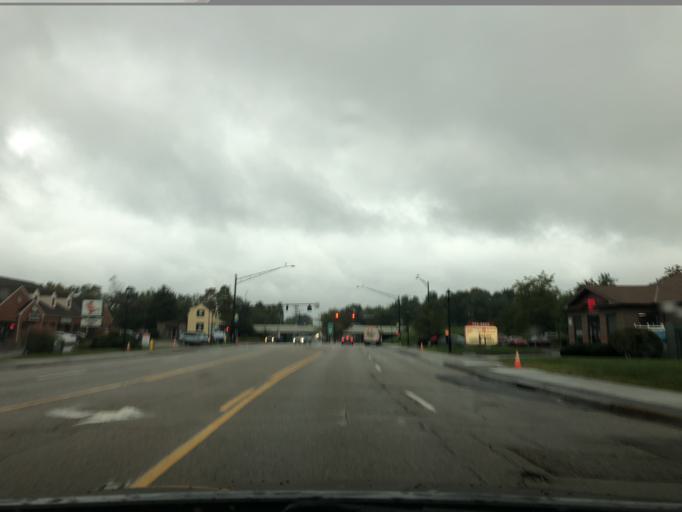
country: US
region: Ohio
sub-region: Hamilton County
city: Blue Ash
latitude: 39.2275
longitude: -84.3774
